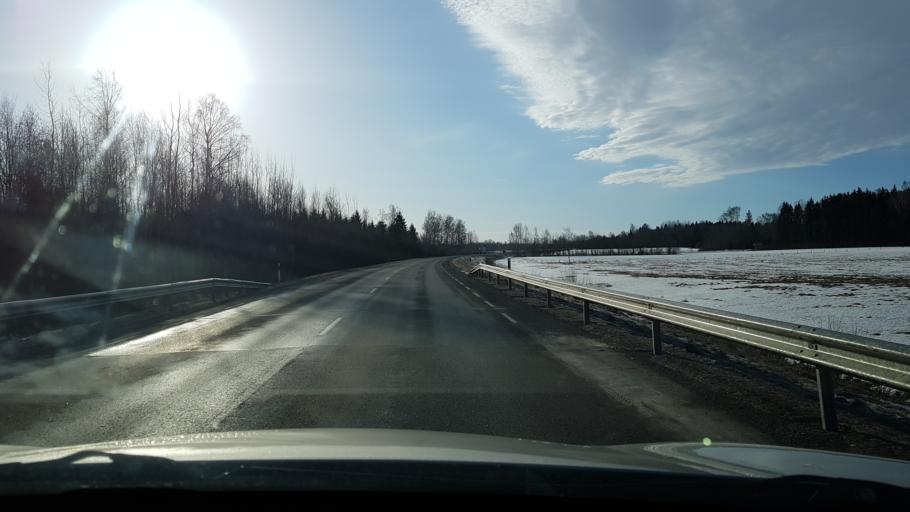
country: EE
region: Viljandimaa
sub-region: Vohma linn
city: Vohma
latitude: 58.5487
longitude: 25.5953
